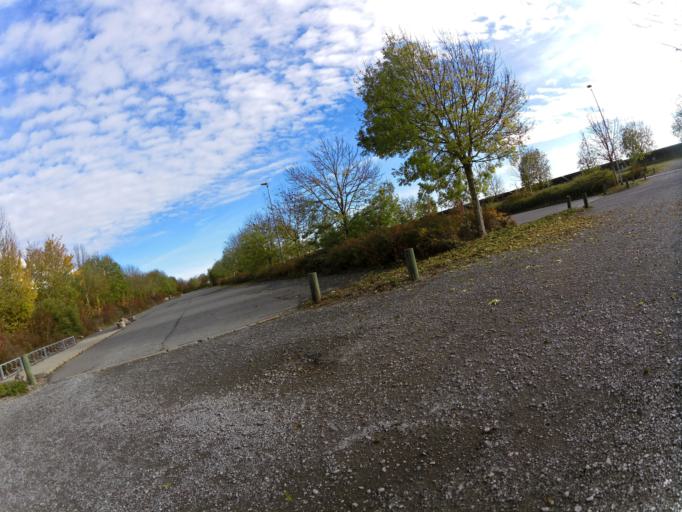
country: DE
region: Bavaria
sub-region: Regierungsbezirk Unterfranken
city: Giebelstadt
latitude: 49.6505
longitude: 9.9558
